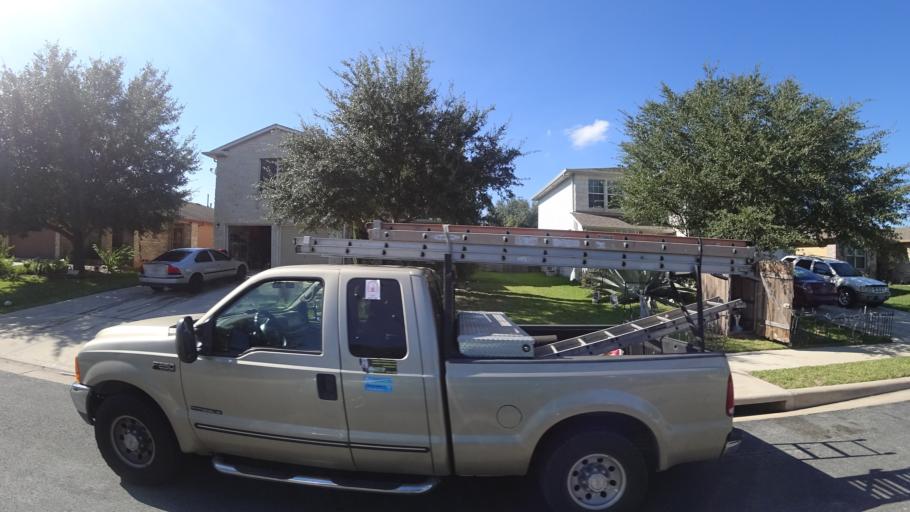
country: US
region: Texas
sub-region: Travis County
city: Manor
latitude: 30.3645
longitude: -97.6088
